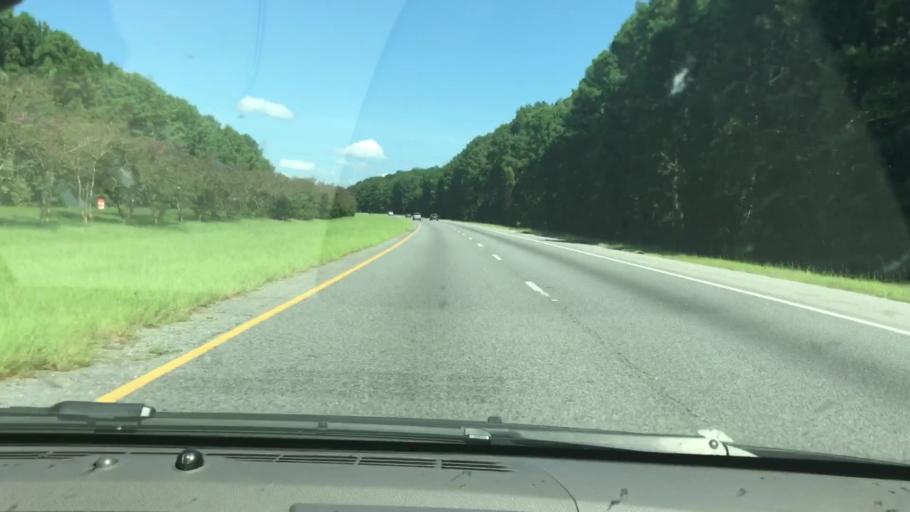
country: US
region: Georgia
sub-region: Harris County
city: Hamilton
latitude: 32.6214
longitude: -84.9530
